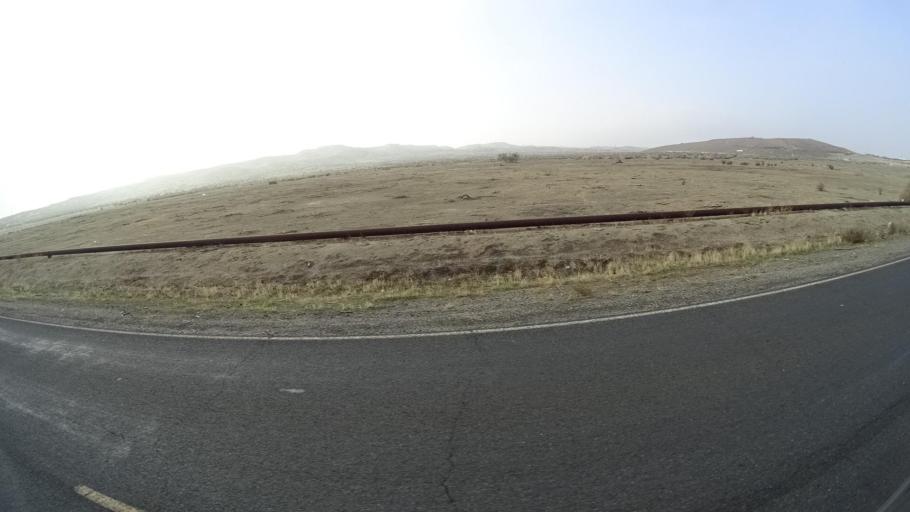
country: US
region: California
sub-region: Kern County
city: Ford City
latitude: 35.1984
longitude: -119.4459
